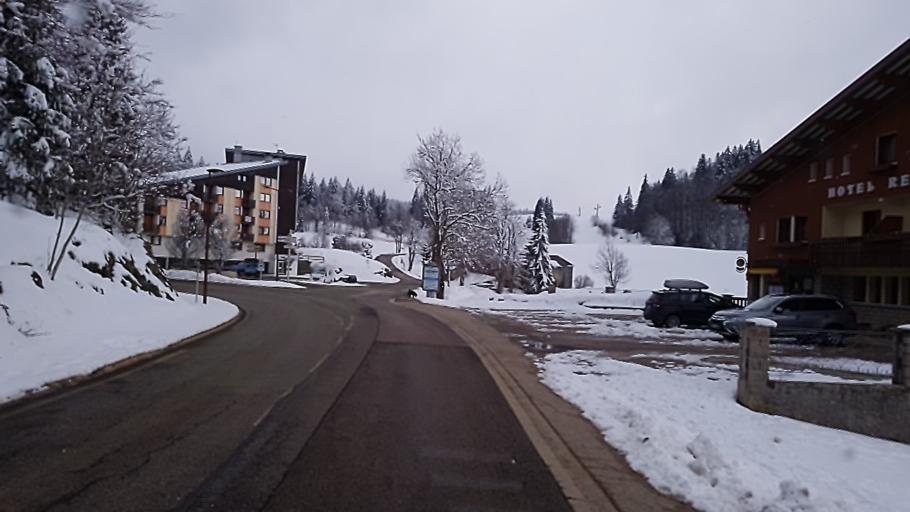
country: FR
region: Franche-Comte
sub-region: Departement du Jura
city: Longchaumois
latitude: 46.3936
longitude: 5.9681
